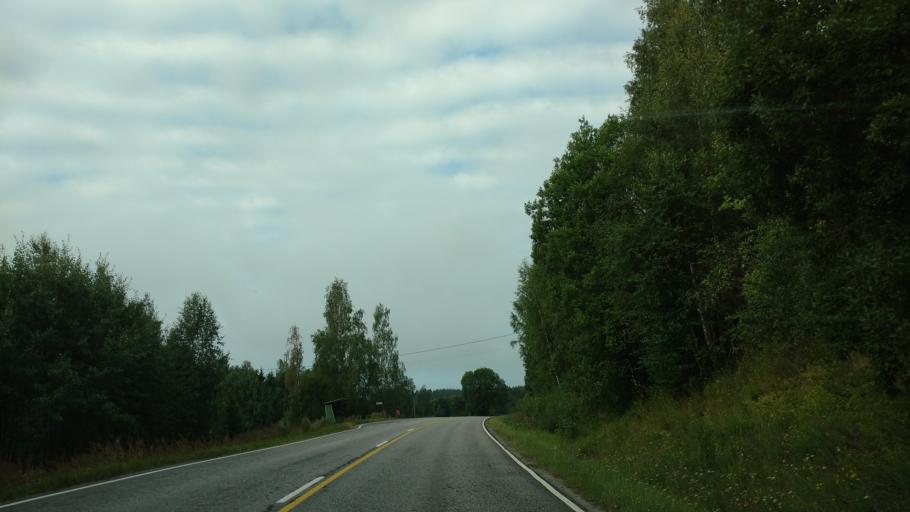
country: FI
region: Varsinais-Suomi
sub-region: Aboland-Turunmaa
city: Kimito
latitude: 60.1480
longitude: 22.6929
